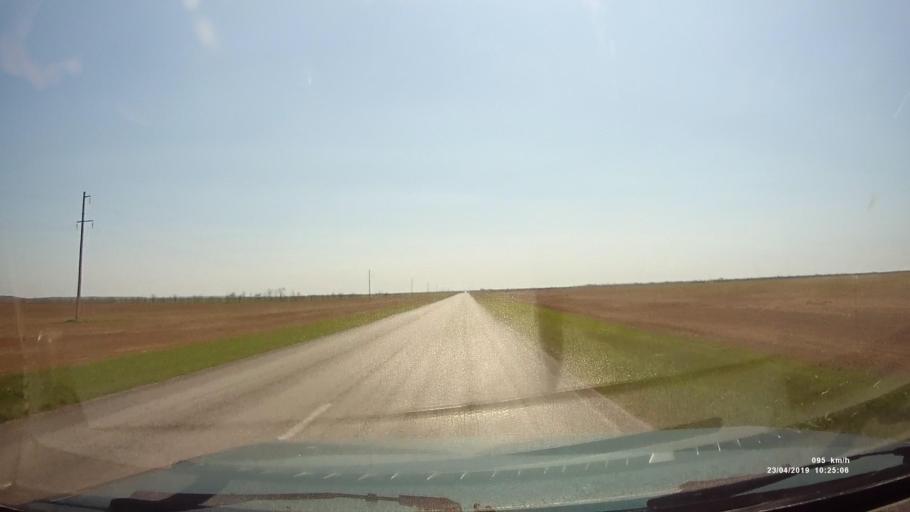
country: RU
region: Rostov
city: Sovetskoye
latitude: 46.6333
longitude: 42.4524
